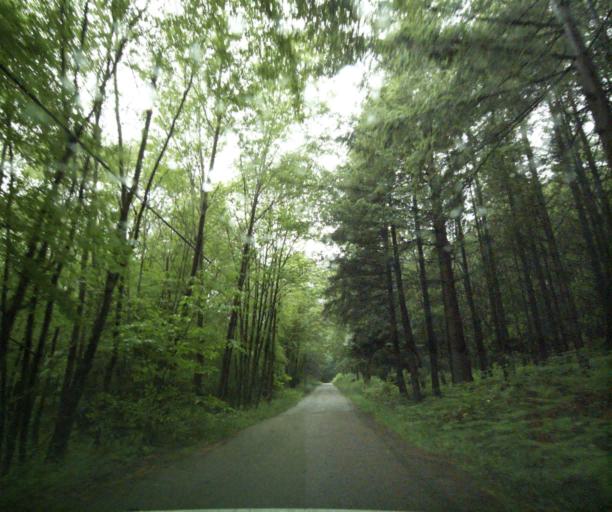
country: FR
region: Bourgogne
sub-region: Departement de Saone-et-Loire
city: Ciry-le-Noble
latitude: 46.5257
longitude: 4.3079
